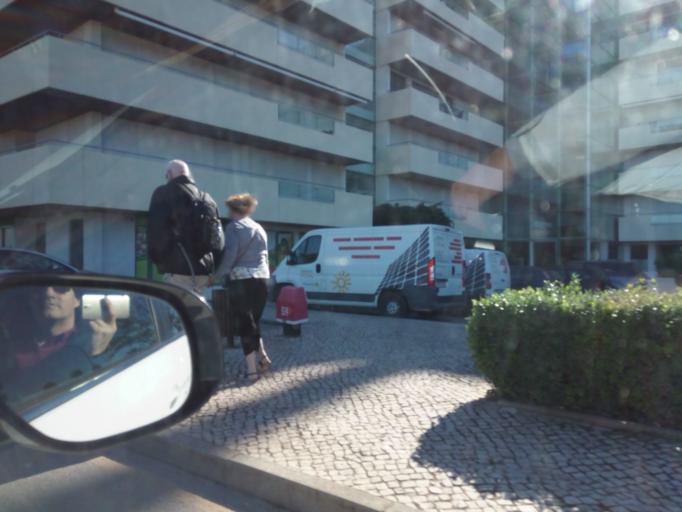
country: PT
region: Faro
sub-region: Loule
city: Vilamoura
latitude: 37.0792
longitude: -8.1232
